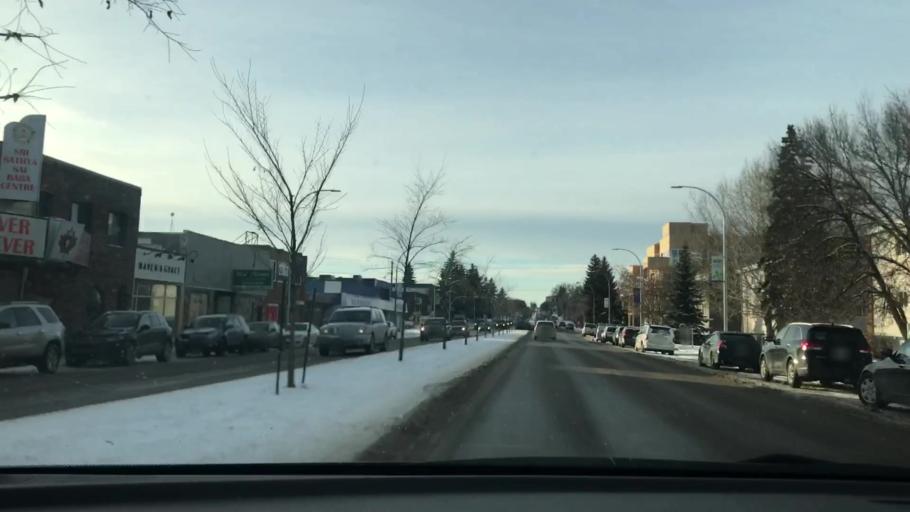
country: CA
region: Alberta
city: Edmonton
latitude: 53.5181
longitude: -113.4775
